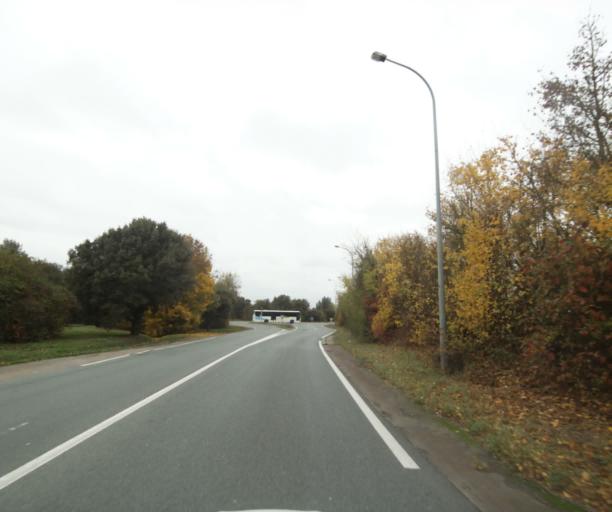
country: FR
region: Poitou-Charentes
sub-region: Departement de la Charente-Maritime
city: Les Gonds
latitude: 45.7231
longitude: -0.6392
